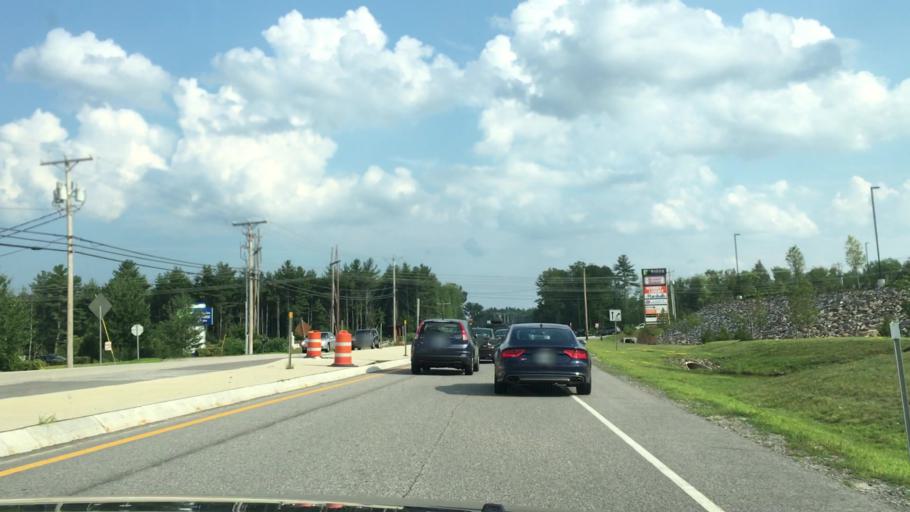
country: US
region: New Hampshire
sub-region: Strafford County
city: Rochester
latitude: 43.3329
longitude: -71.0077
